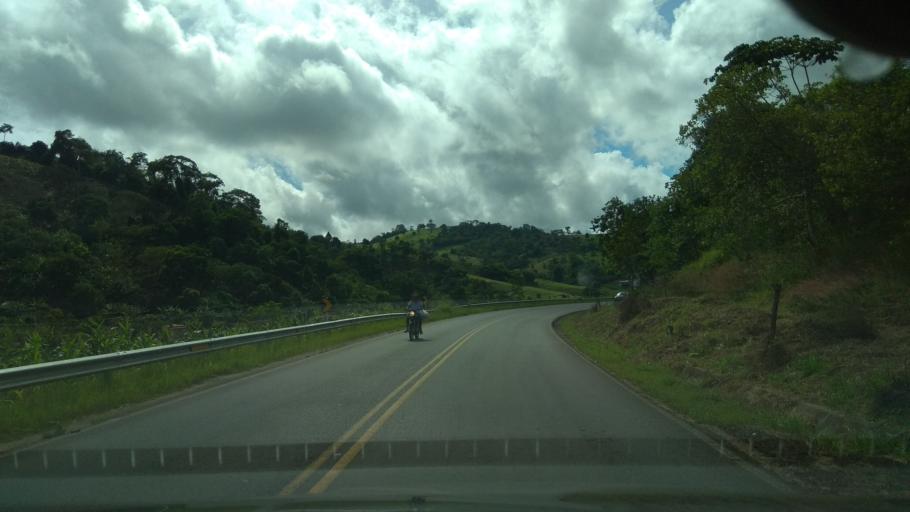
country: BR
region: Bahia
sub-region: Mutuipe
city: Mutuipe
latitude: -13.1837
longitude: -39.4397
